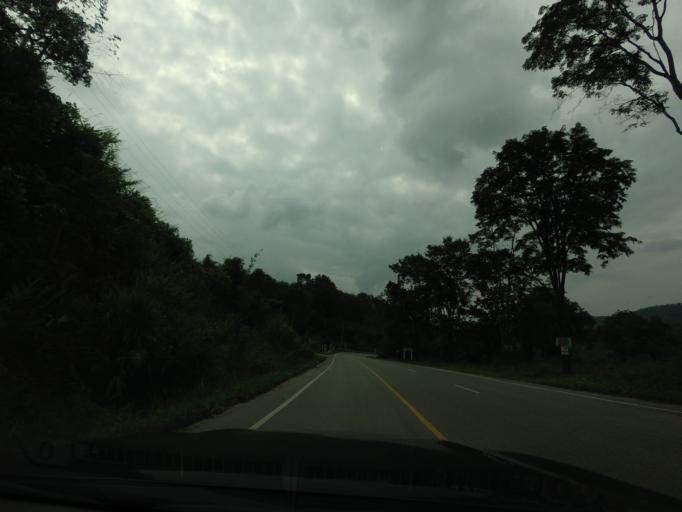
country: TH
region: Loei
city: Dan Sai
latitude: 17.2237
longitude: 101.1884
